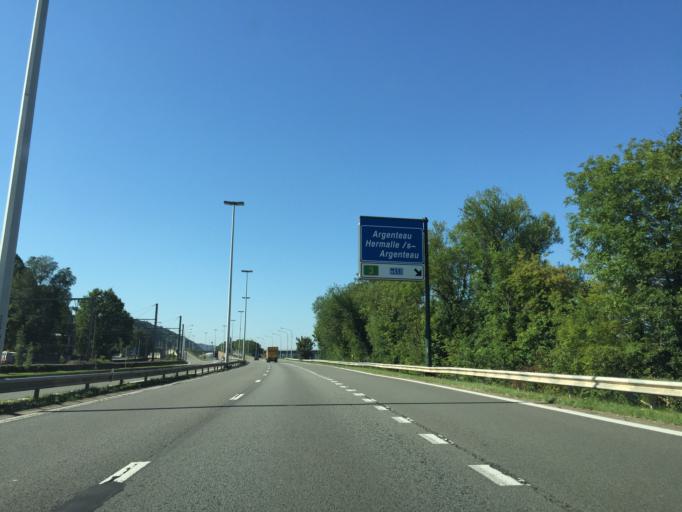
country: BE
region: Wallonia
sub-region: Province de Liege
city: Vise
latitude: 50.7147
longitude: 5.6869
